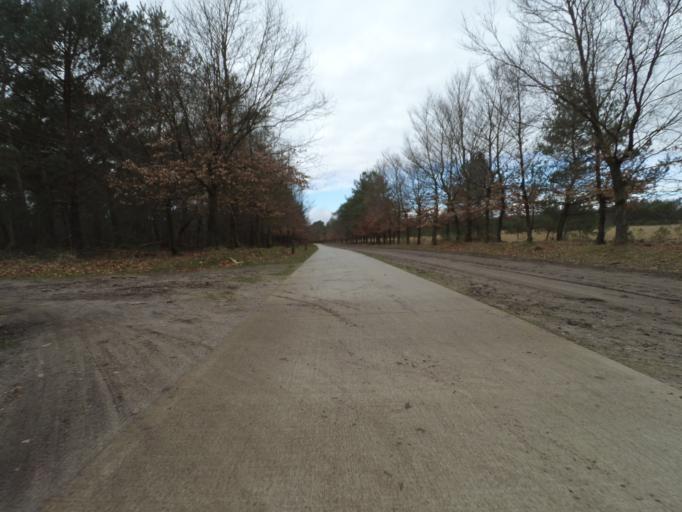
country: NL
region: Gelderland
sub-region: Gemeente Rozendaal
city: Rozendaal
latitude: 52.0498
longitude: 5.9427
